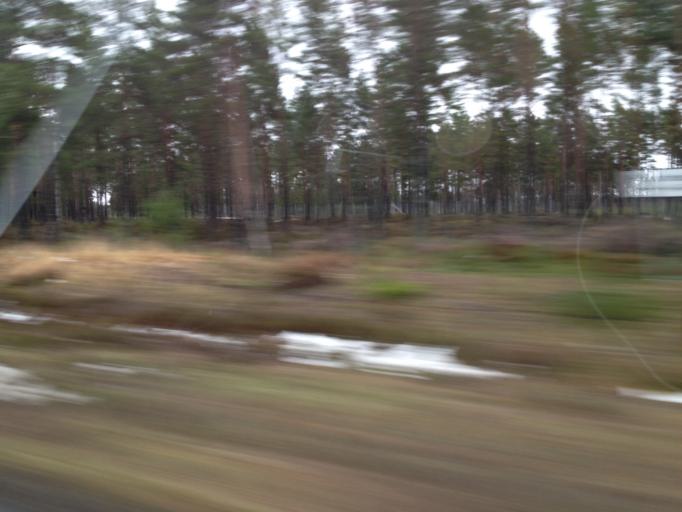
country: FI
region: Uusimaa
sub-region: Raaseporin
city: Hanko
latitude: 59.8499
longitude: 23.0051
